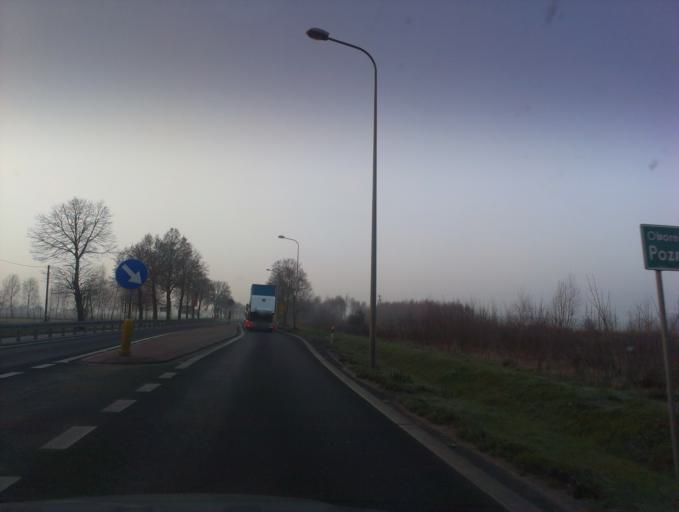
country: PL
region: Greater Poland Voivodeship
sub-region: Powiat obornicki
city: Rogozno
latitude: 52.7585
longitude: 16.9640
